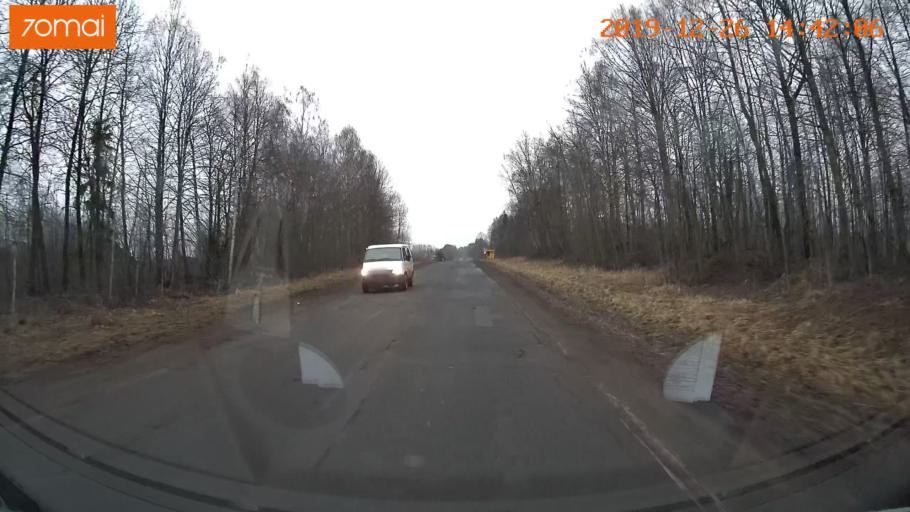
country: RU
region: Jaroslavl
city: Poshekhon'ye
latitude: 58.3663
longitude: 39.0267
